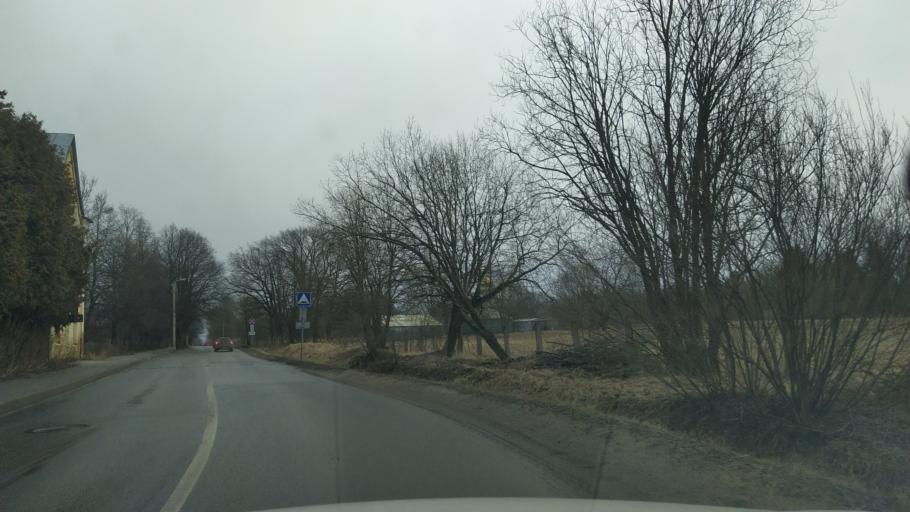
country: RU
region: St.-Petersburg
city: Pushkin
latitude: 59.7288
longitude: 30.3866
